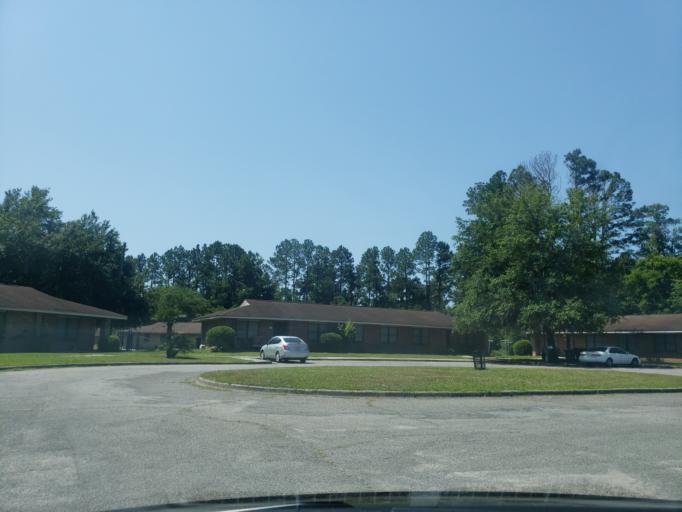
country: US
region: Georgia
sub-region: Chatham County
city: Montgomery
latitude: 31.9956
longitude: -81.1356
